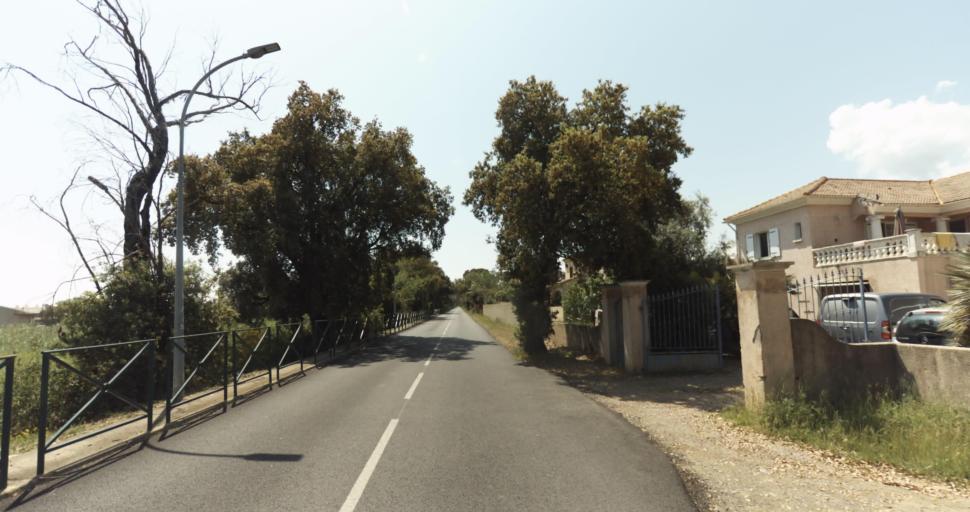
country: FR
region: Corsica
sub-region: Departement de la Haute-Corse
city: Biguglia
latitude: 42.6043
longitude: 9.4340
